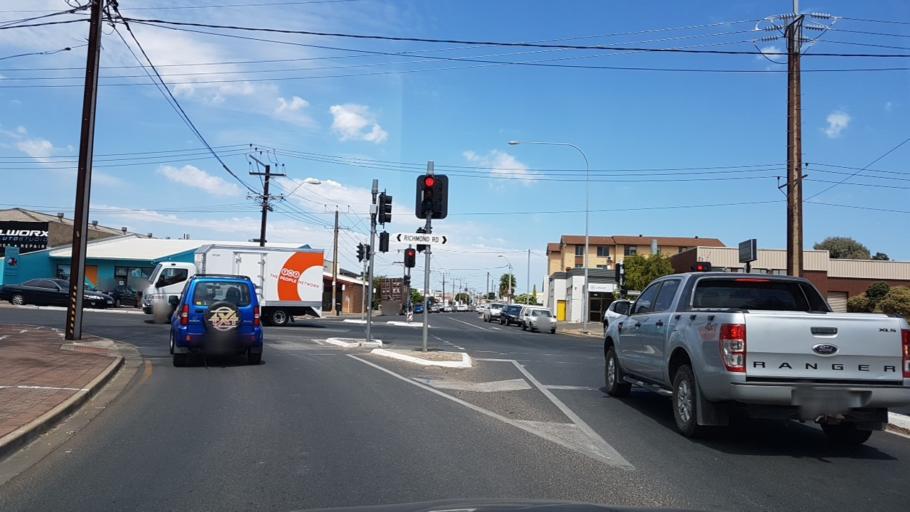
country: AU
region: South Australia
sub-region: Unley
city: Forestville
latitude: -34.9415
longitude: 138.5780
